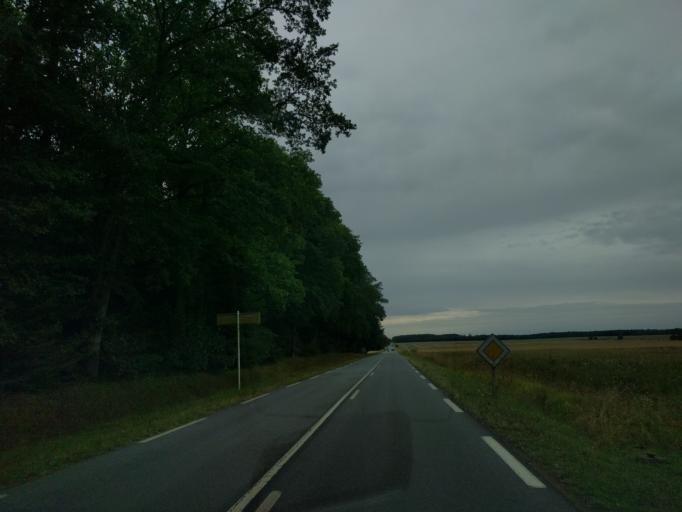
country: FR
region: Haute-Normandie
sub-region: Departement de l'Eure
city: Saint-Sebastien-de-Morsent
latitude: 49.0048
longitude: 1.0666
